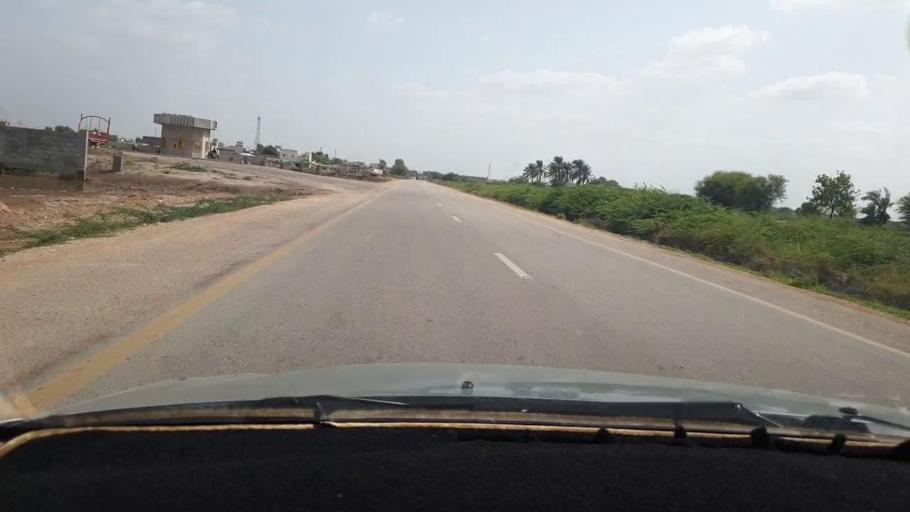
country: PK
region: Sindh
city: Naukot
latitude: 24.9822
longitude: 69.2936
